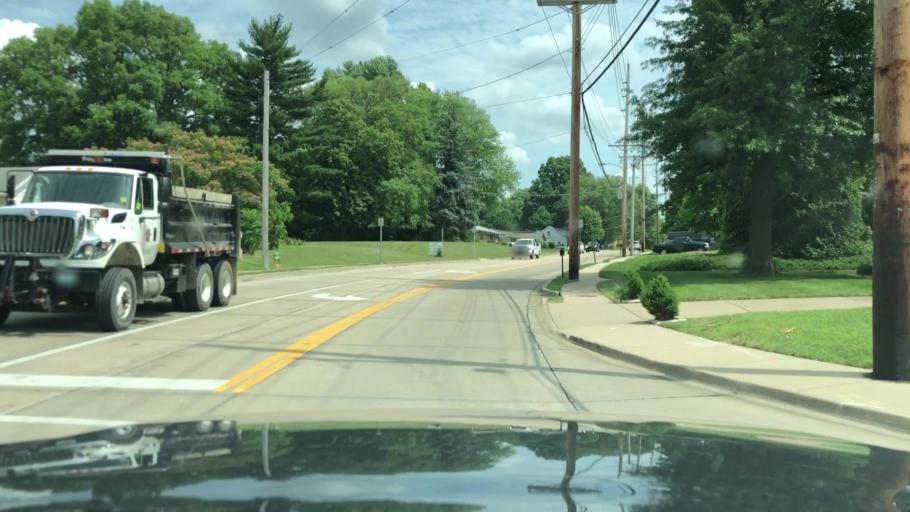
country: US
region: Missouri
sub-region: Saint Charles County
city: Saint Charles
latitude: 38.8063
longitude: -90.5090
